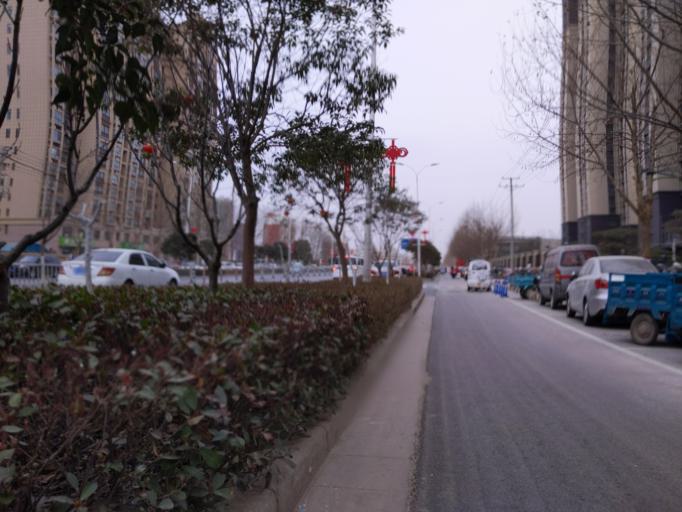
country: CN
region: Henan Sheng
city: Zhongyuanlu
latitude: 35.7575
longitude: 115.0750
